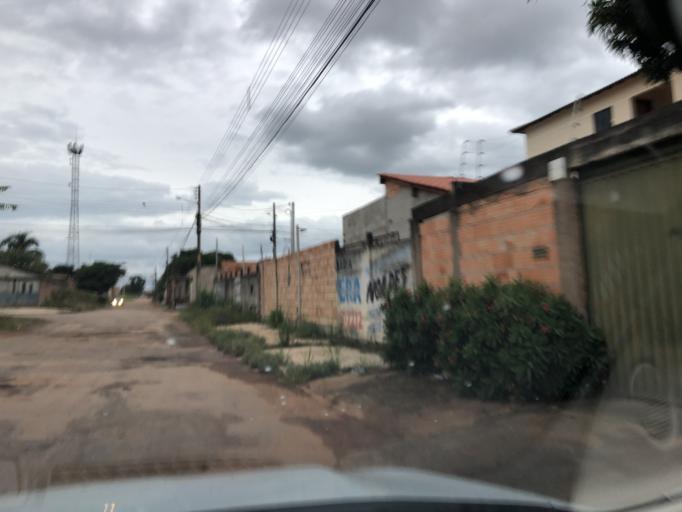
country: BR
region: Goias
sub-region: Luziania
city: Luziania
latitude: -16.1516
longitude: -47.9424
